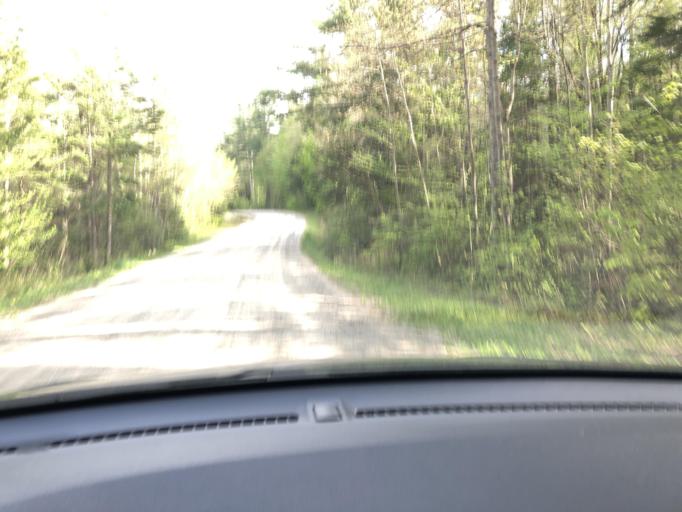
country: US
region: New Hampshire
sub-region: Merrimack County
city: New London
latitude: 43.4032
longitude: -72.0141
